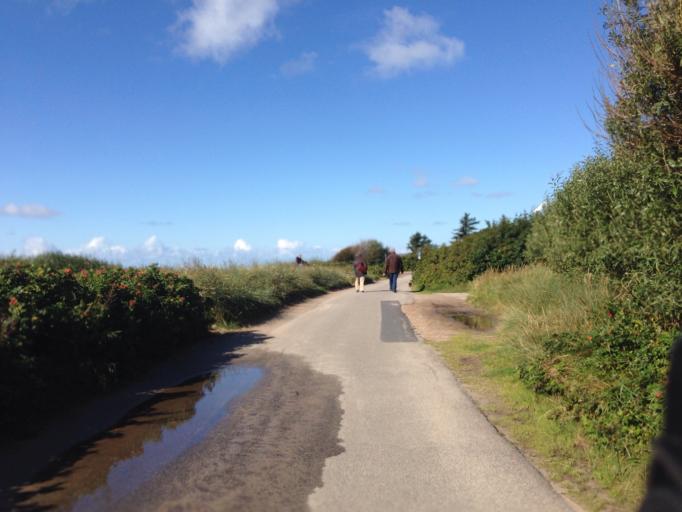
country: DE
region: Schleswig-Holstein
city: Borgsum
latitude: 54.6840
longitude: 8.4691
